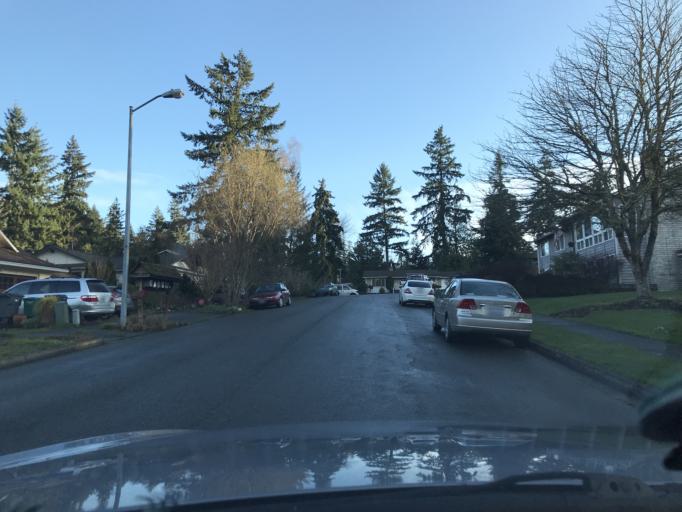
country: US
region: Washington
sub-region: King County
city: Sammamish
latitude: 47.6396
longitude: -122.1020
